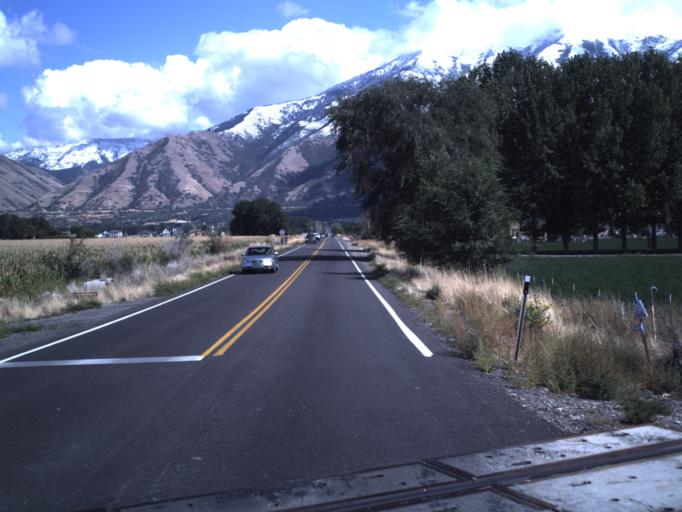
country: US
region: Utah
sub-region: Utah County
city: Mapleton
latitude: 40.1155
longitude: -111.6066
